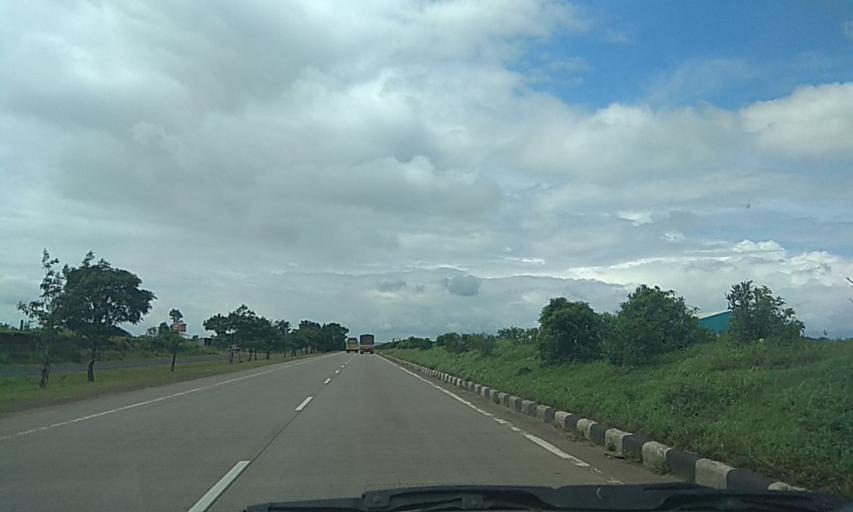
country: IN
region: Maharashtra
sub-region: Kolhapur
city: Kagal
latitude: 16.5075
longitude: 74.3312
